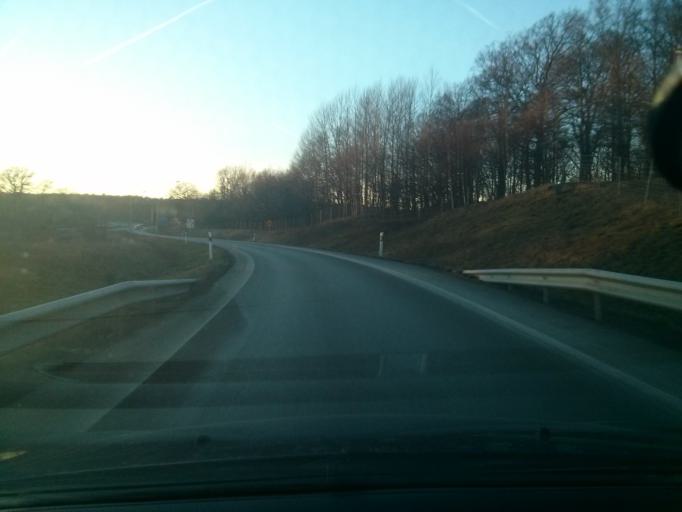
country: SE
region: Blekinge
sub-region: Karlskrona Kommun
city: Rodeby
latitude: 56.2137
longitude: 15.5917
